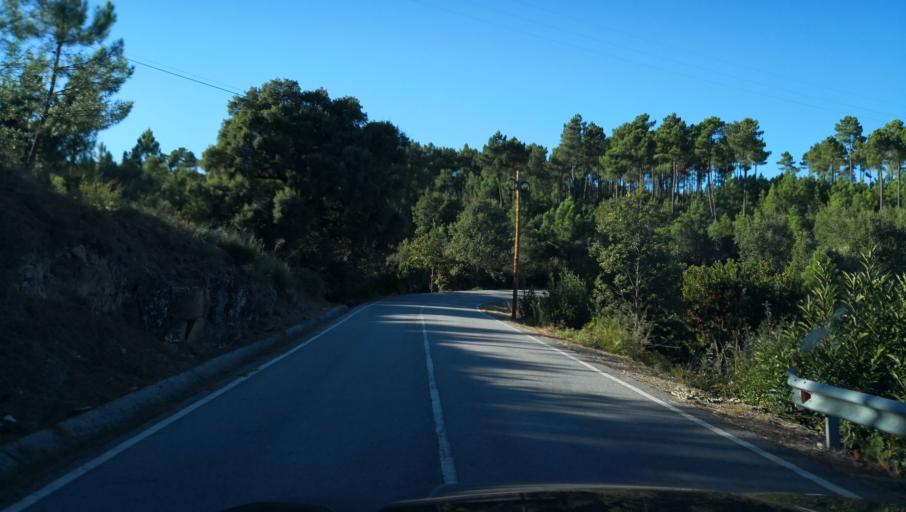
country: PT
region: Vila Real
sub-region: Sabrosa
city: Sabrosa
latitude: 41.3021
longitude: -7.5783
